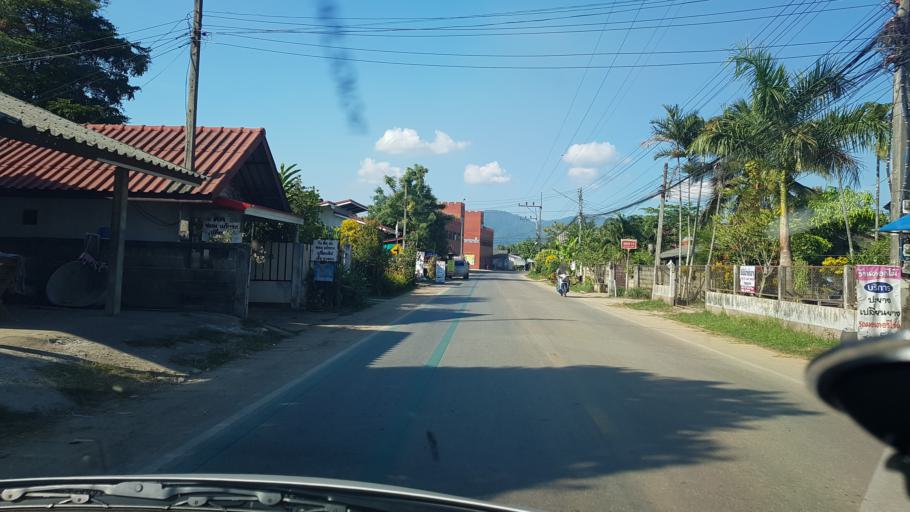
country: TH
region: Chiang Rai
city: Chiang Rai
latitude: 19.9488
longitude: 99.8099
